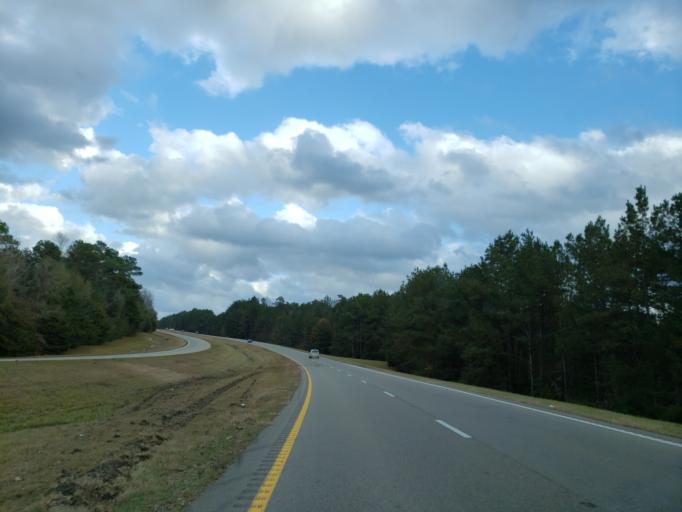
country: US
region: Mississippi
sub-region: Perry County
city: New Augusta
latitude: 31.2112
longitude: -89.1620
